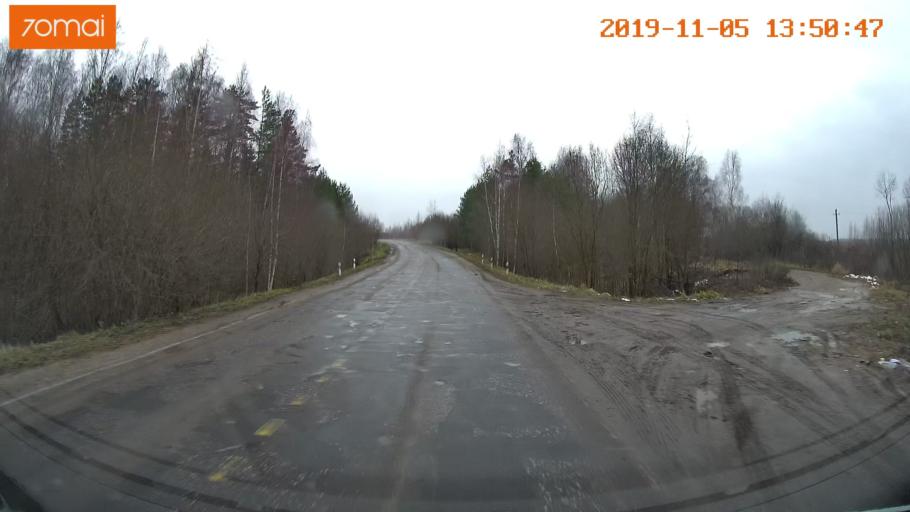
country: RU
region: Ivanovo
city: Kaminskiy
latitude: 57.0219
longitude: 41.4062
